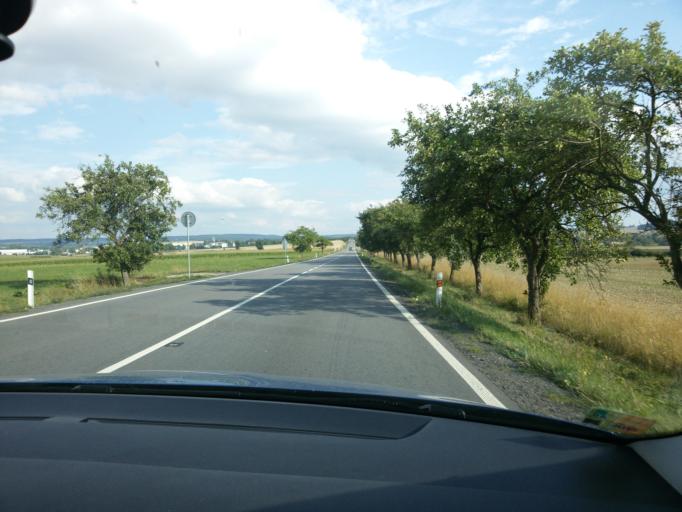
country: CZ
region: Pardubicky
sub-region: Okres Svitavy
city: Policka
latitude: 49.7249
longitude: 16.2317
